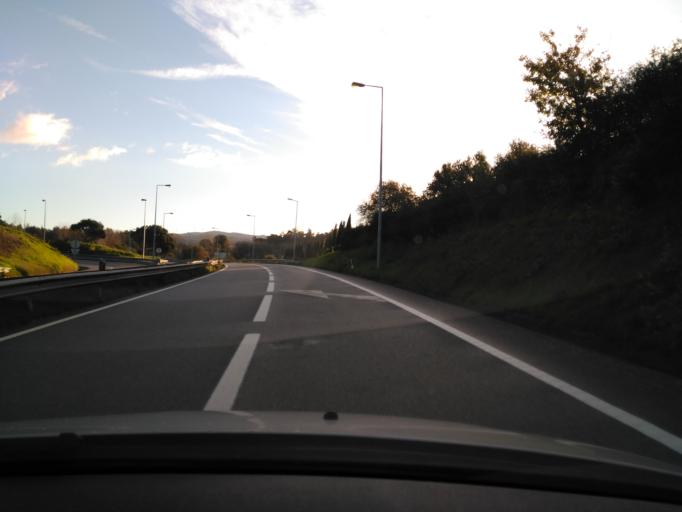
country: PT
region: Braga
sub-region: Fafe
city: Fafe
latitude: 41.4636
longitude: -8.1730
